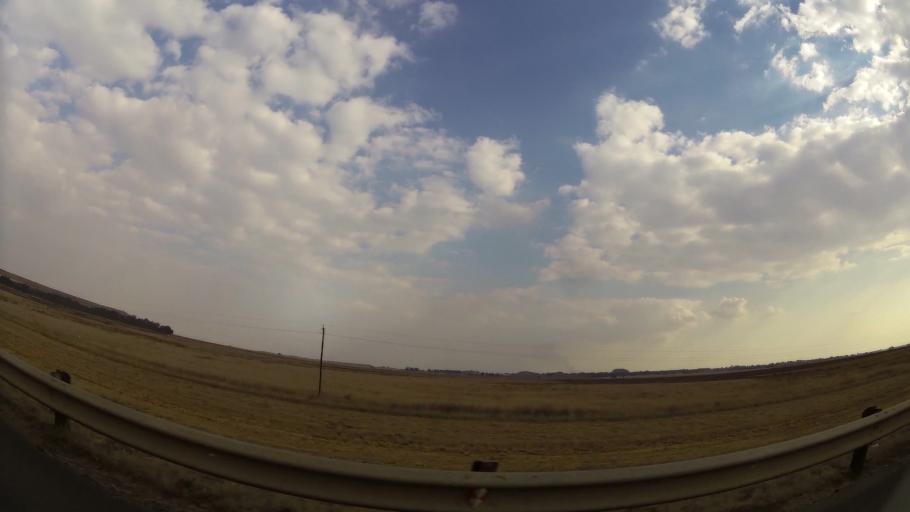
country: ZA
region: Gauteng
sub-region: Ekurhuleni Metropolitan Municipality
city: Springs
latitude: -26.2769
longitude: 28.5179
